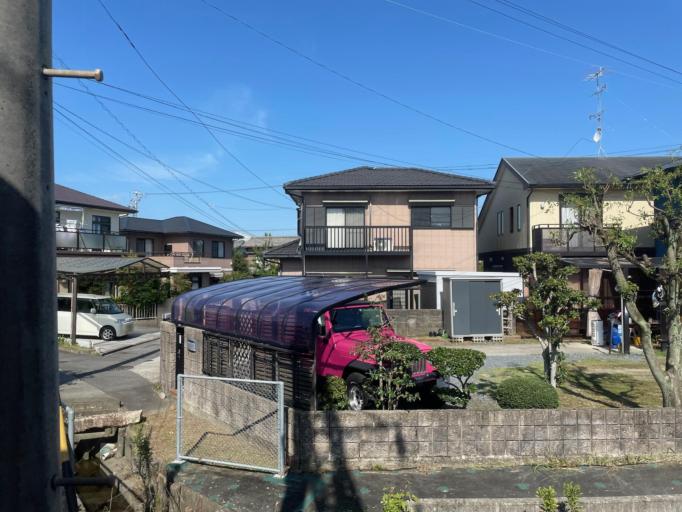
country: JP
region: Mie
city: Yokkaichi
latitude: 34.9695
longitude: 136.5914
